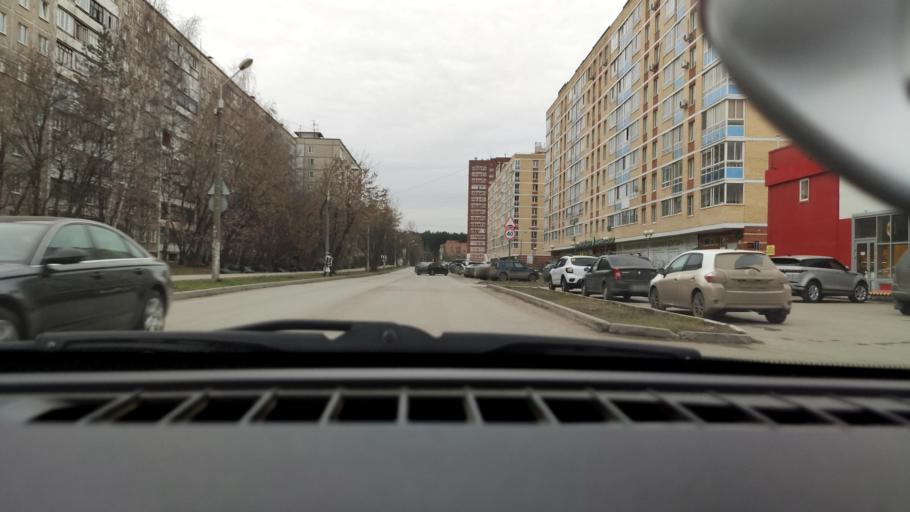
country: RU
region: Perm
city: Kondratovo
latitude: 57.9964
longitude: 56.1476
